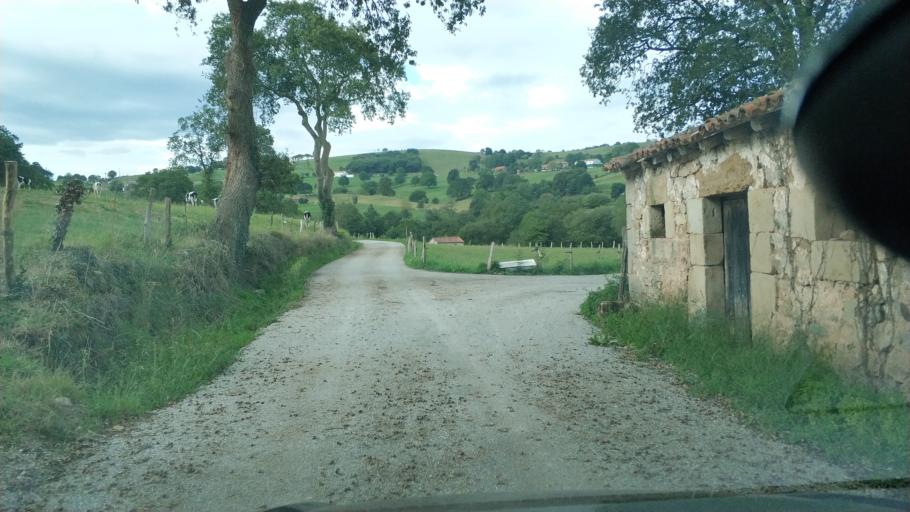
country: ES
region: Cantabria
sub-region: Provincia de Cantabria
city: Santa Maria de Cayon
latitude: 43.2812
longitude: -3.8103
